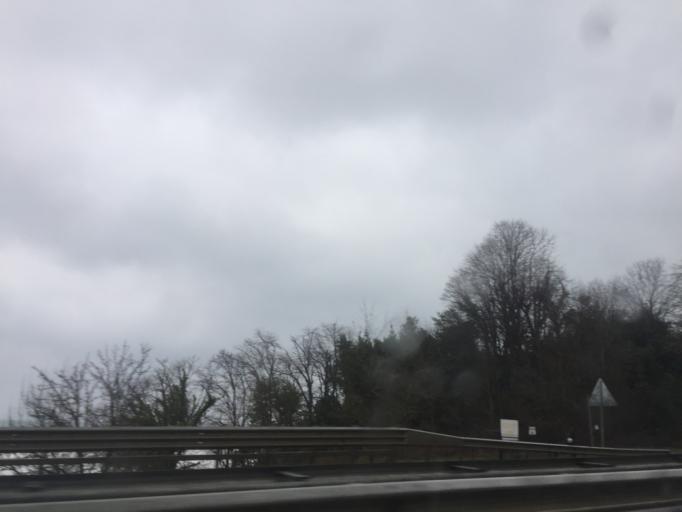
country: TR
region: Duzce
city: Akcakoca
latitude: 41.1013
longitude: 31.2385
